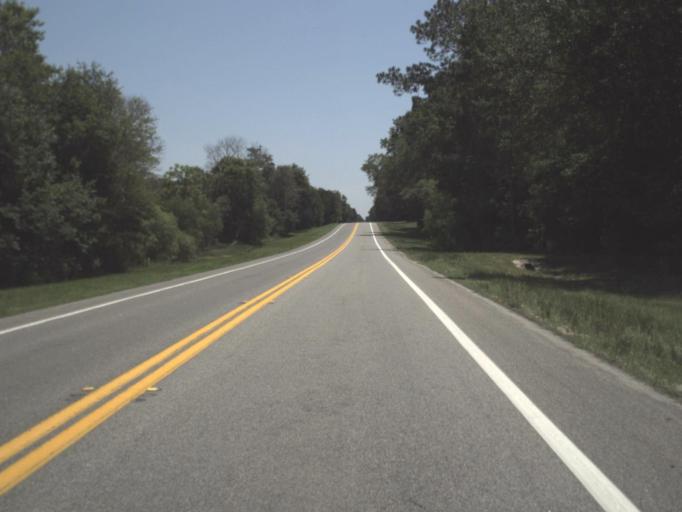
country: US
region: Florida
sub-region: Suwannee County
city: Live Oak
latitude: 30.3300
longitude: -83.0604
